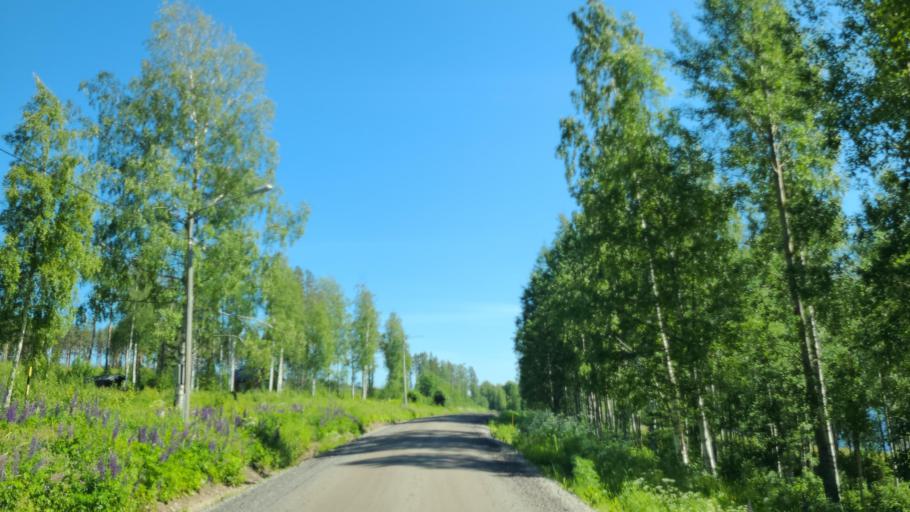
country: SE
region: Vaesterbotten
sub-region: Bjurholms Kommun
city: Bjurholm
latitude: 63.6712
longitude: 19.0617
